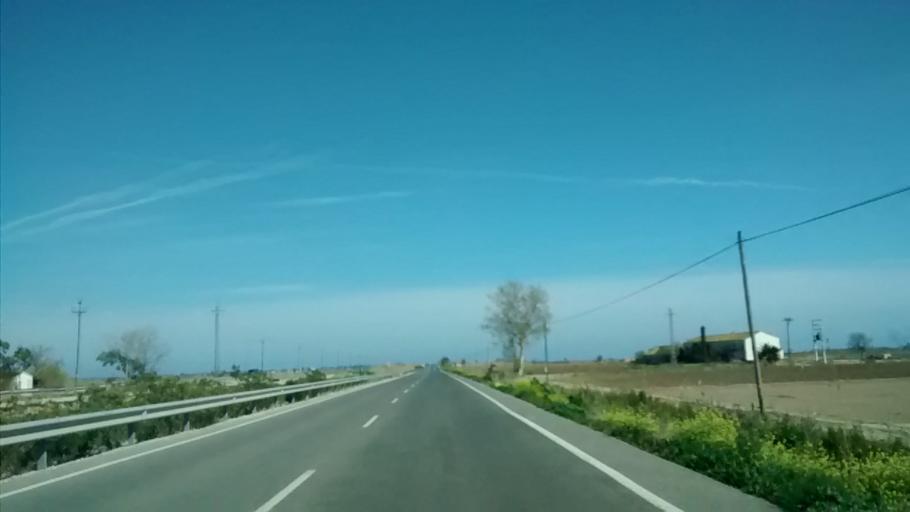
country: ES
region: Catalonia
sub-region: Provincia de Tarragona
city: Deltebre
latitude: 40.7063
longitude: 0.7696
